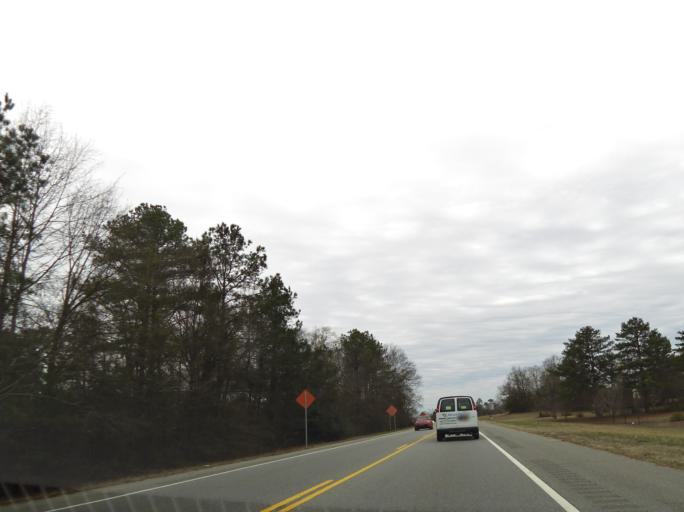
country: US
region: Georgia
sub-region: Bibb County
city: West Point
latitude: 32.8041
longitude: -83.8115
